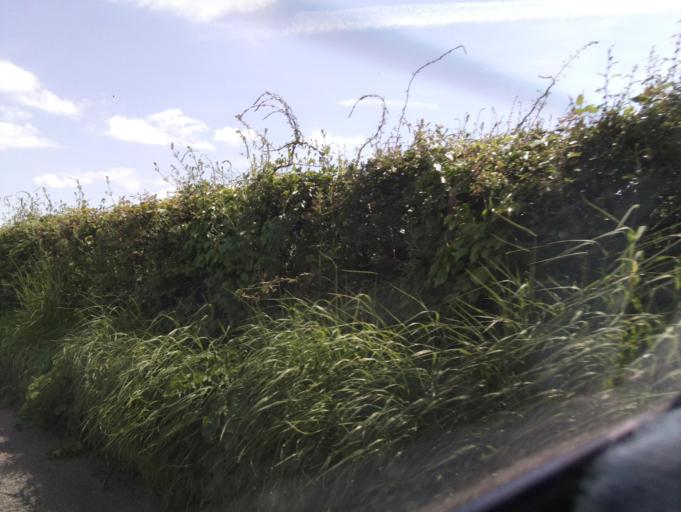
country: GB
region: England
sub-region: Herefordshire
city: Llanrothal
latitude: 51.8472
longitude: -2.7895
